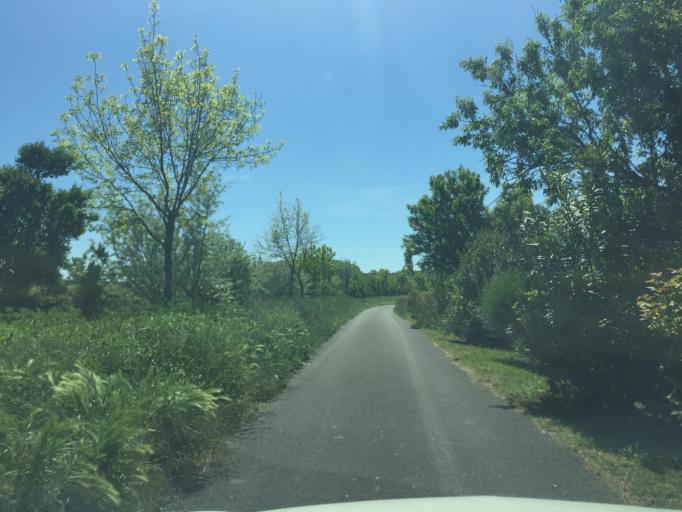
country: FR
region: Provence-Alpes-Cote d'Azur
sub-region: Departement du Vaucluse
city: Caderousse
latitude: 44.1008
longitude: 4.7881
